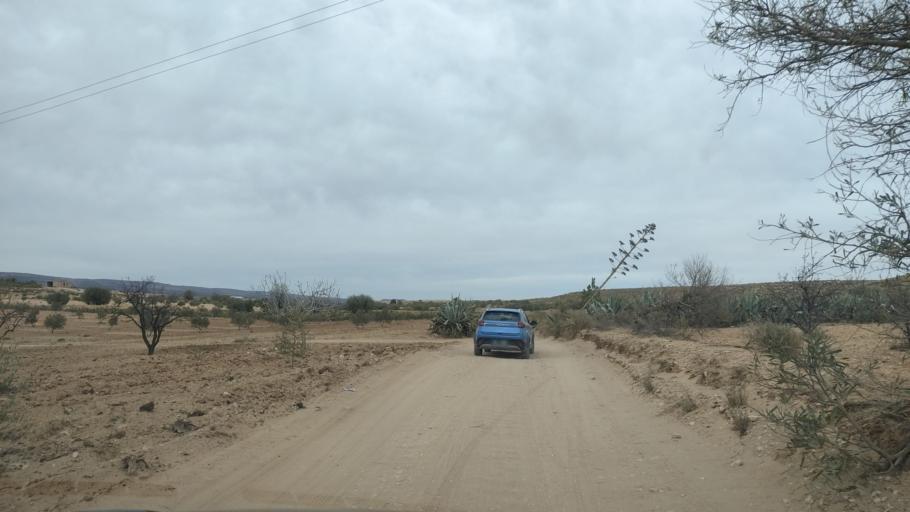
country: TN
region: Al Qasrayn
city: Kasserine
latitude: 35.2497
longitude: 8.9208
